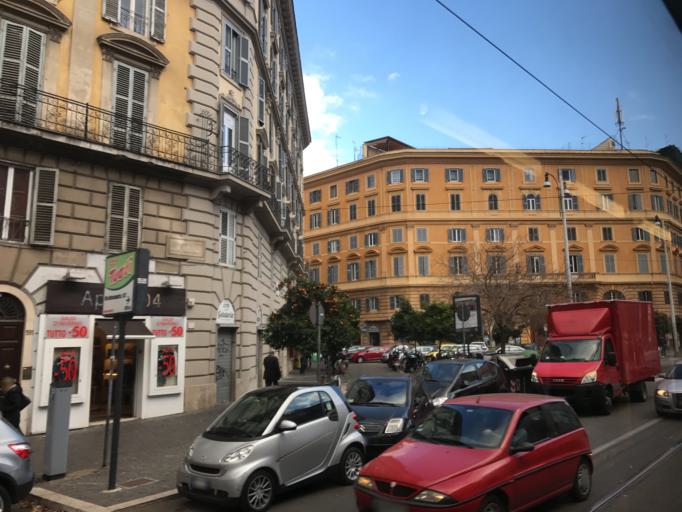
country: IT
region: Latium
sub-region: Citta metropolitana di Roma Capitale
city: Rome
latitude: 41.9144
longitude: 12.5047
